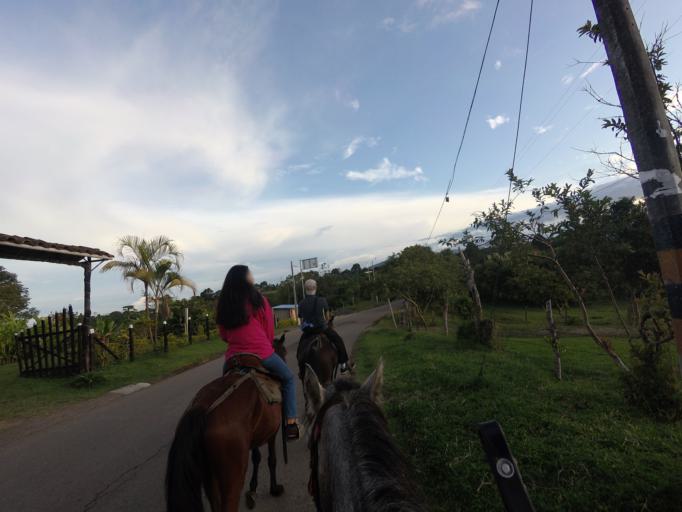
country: CO
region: Huila
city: San Agustin
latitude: 1.8944
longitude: -76.2729
